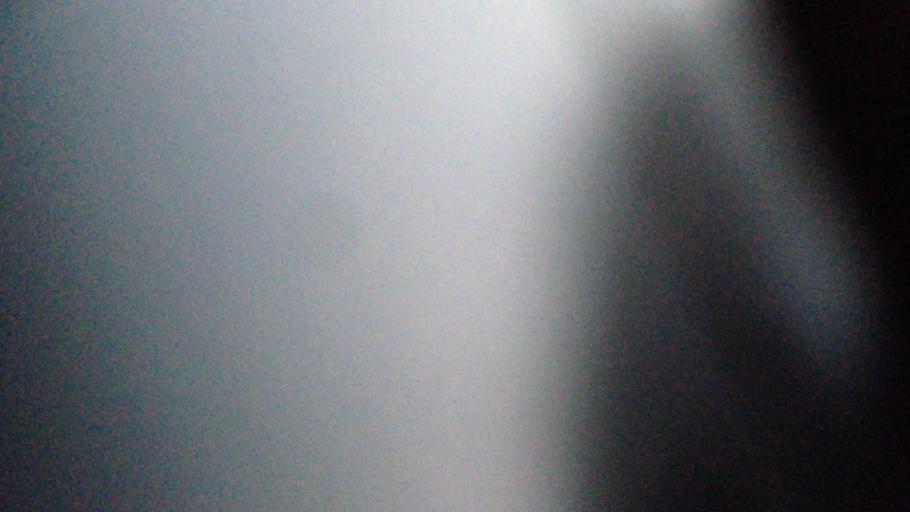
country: US
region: New York
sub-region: Greene County
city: Catskill
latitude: 42.2229
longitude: -73.8271
